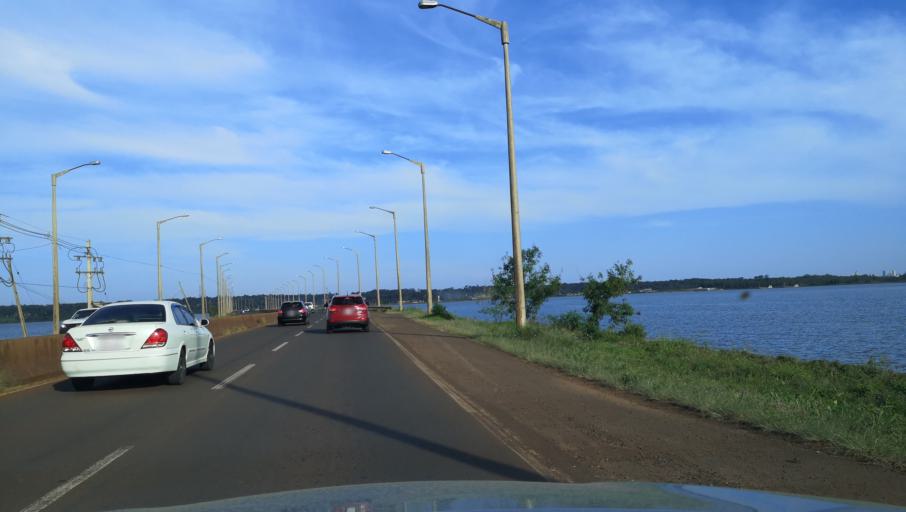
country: PY
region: Itapua
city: San Juan del Parana
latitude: -27.2936
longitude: -55.9107
